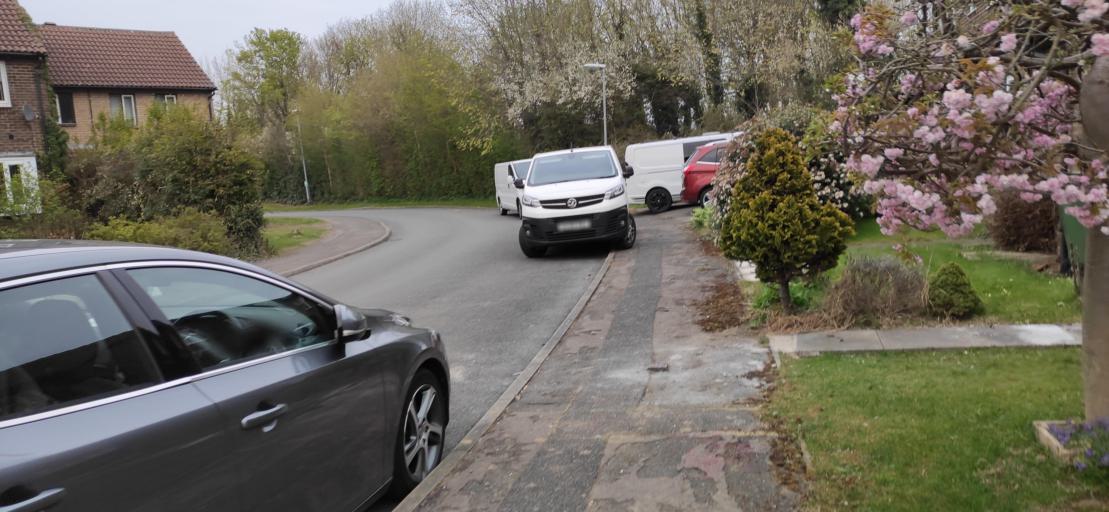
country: GB
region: England
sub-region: Cambridgeshire
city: Swavesey
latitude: 52.2498
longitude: 0.0184
